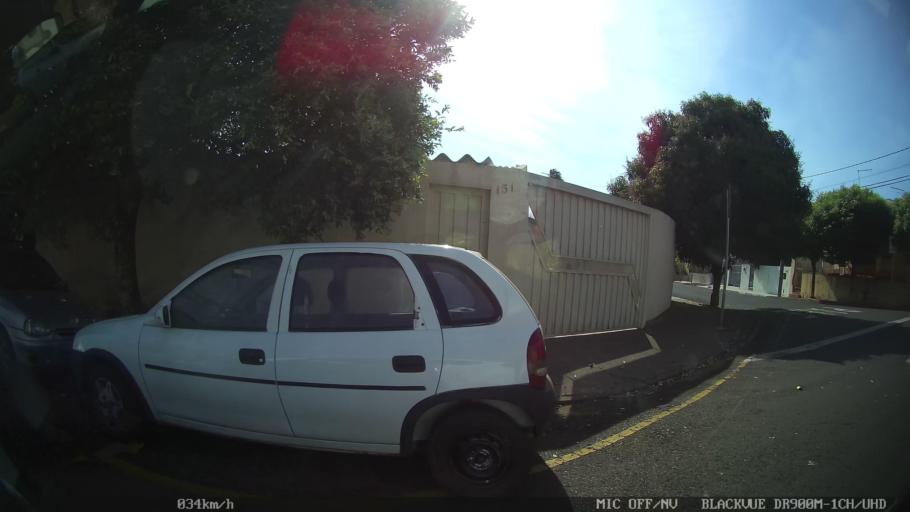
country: BR
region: Sao Paulo
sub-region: Sao Jose Do Rio Preto
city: Sao Jose do Rio Preto
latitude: -20.7972
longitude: -49.4215
